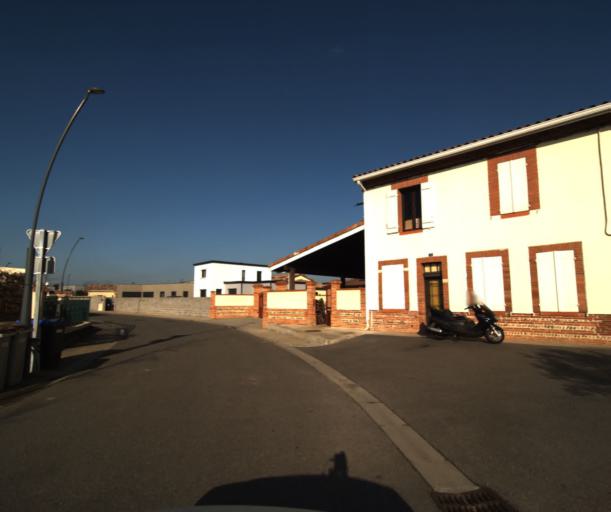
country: FR
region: Midi-Pyrenees
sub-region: Departement de la Haute-Garonne
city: Colomiers
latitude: 43.5950
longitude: 1.3589
